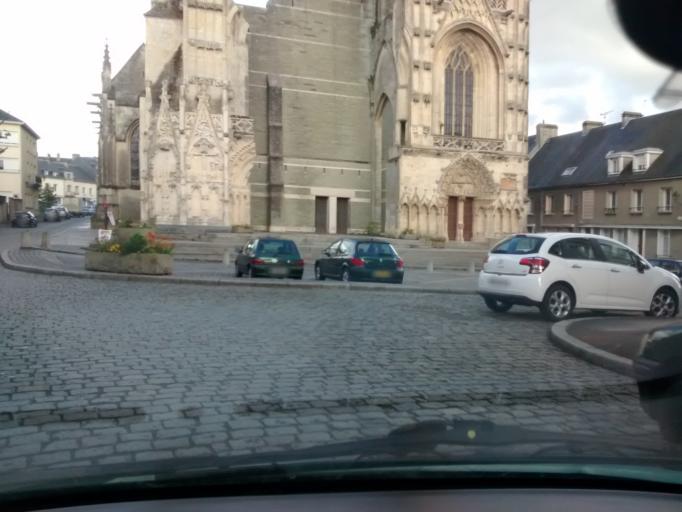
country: FR
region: Lower Normandy
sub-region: Departement de la Manche
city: Saint-Lo
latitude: 49.1155
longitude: -1.0952
